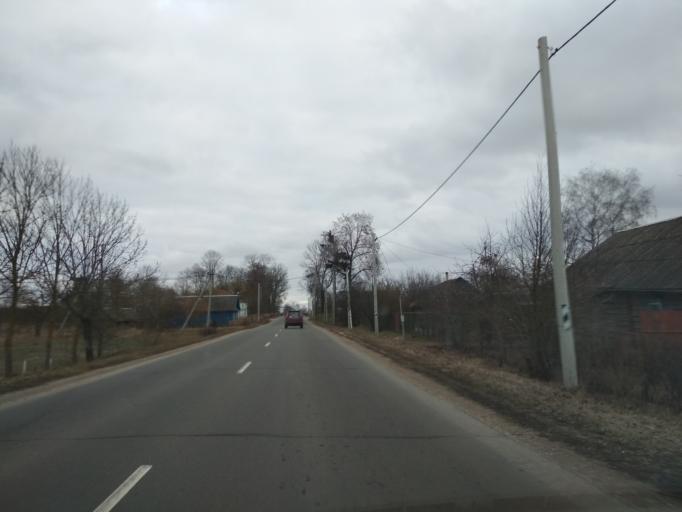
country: BY
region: Minsk
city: Svislach
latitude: 53.5702
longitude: 27.9768
